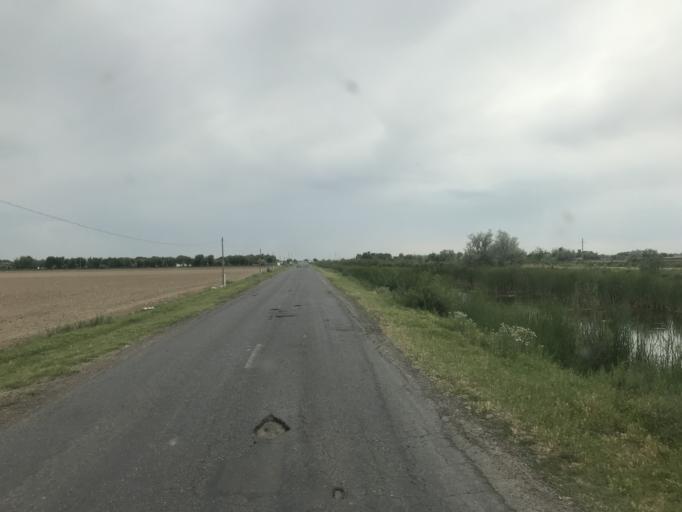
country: KZ
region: Ongtustik Qazaqstan
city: Asykata
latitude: 40.9189
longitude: 68.3985
